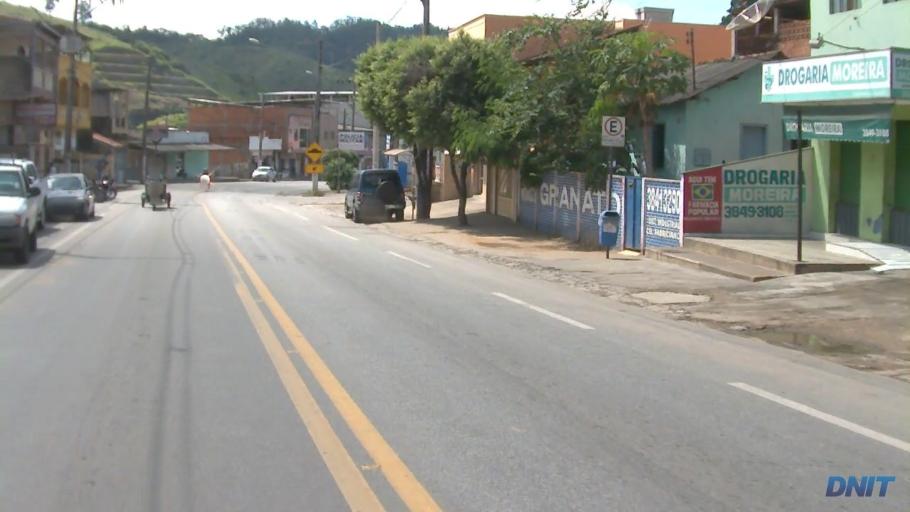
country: BR
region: Minas Gerais
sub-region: Coronel Fabriciano
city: Coronel Fabriciano
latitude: -19.5324
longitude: -42.6676
